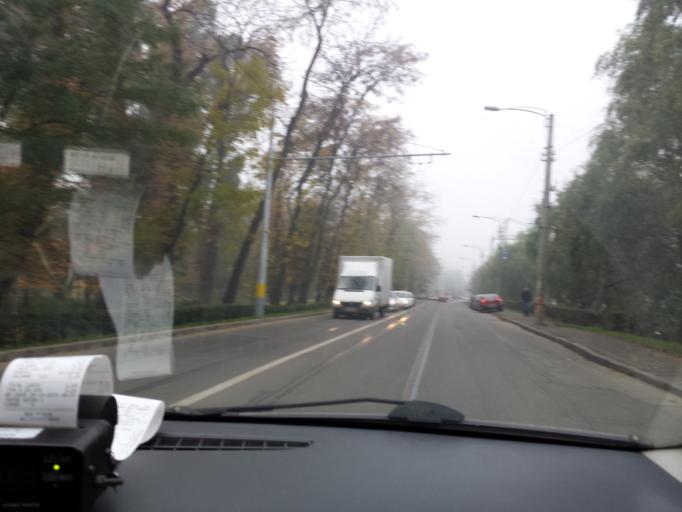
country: RO
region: Cluj
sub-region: Municipiul Cluj-Napoca
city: Cluj-Napoca
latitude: 46.7707
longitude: 23.5778
